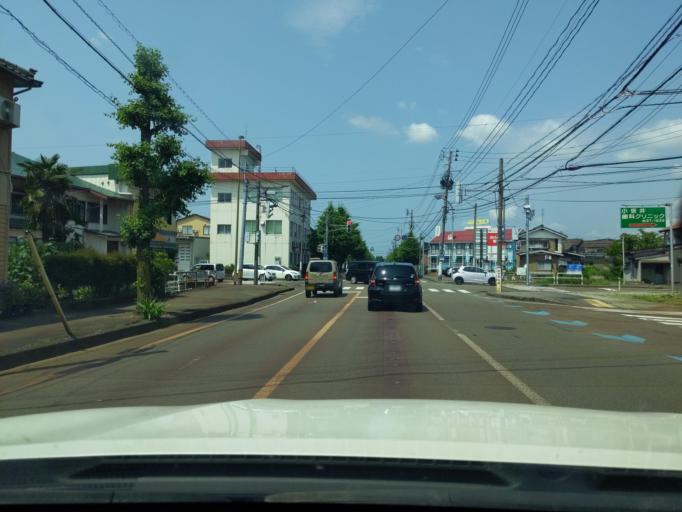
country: JP
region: Niigata
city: Nagaoka
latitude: 37.4308
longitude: 138.8521
